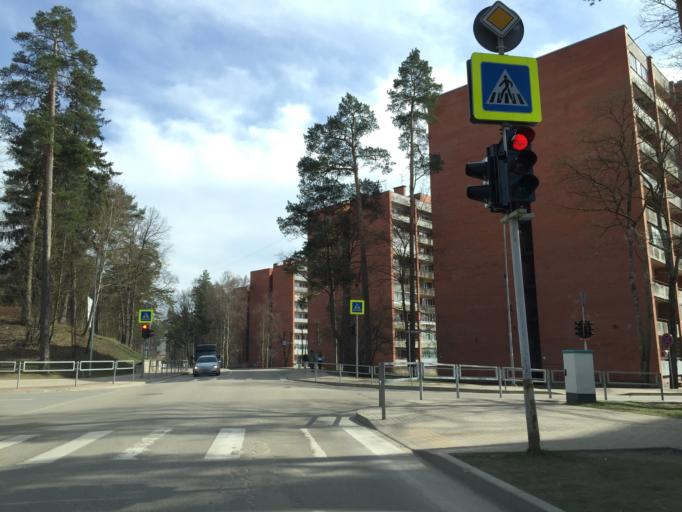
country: LV
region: Ogre
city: Ogre
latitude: 56.8226
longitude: 24.6021
